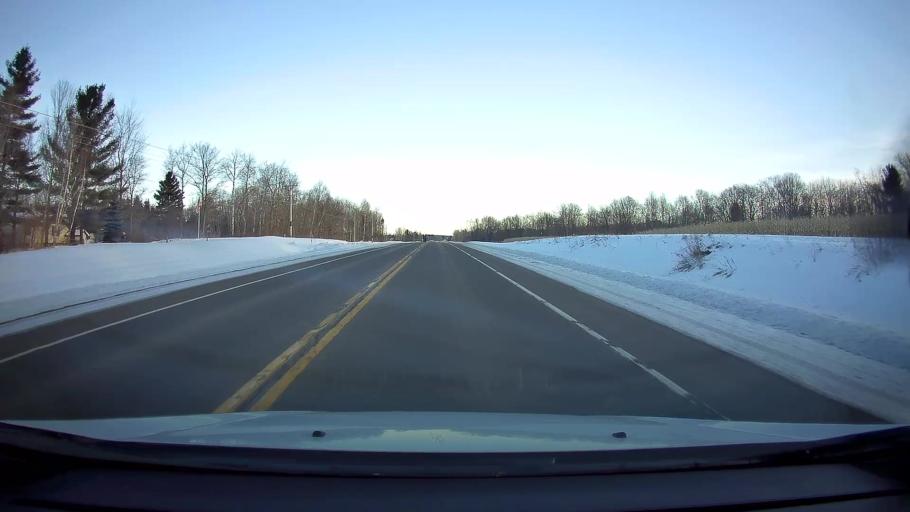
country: US
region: Wisconsin
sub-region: Barron County
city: Cumberland
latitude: 45.6075
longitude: -92.0127
